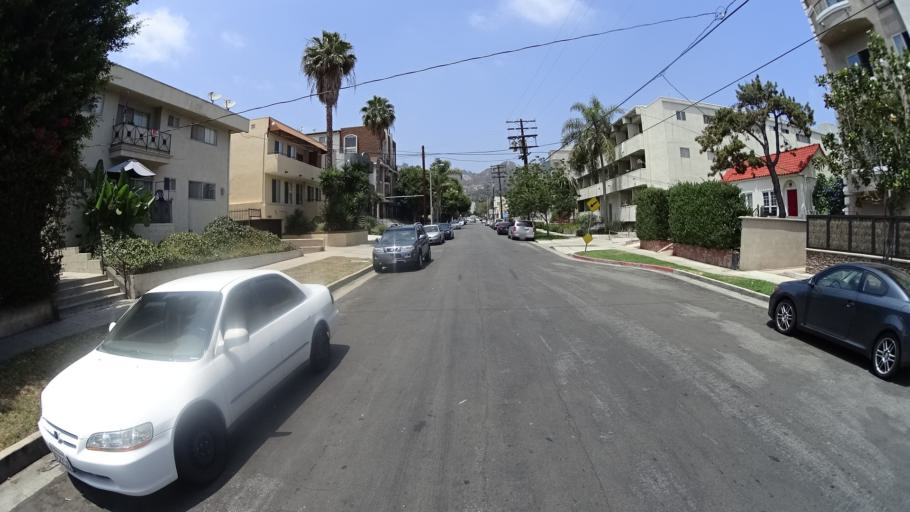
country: US
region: California
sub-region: Los Angeles County
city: West Hollywood
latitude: 34.0965
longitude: -118.3550
